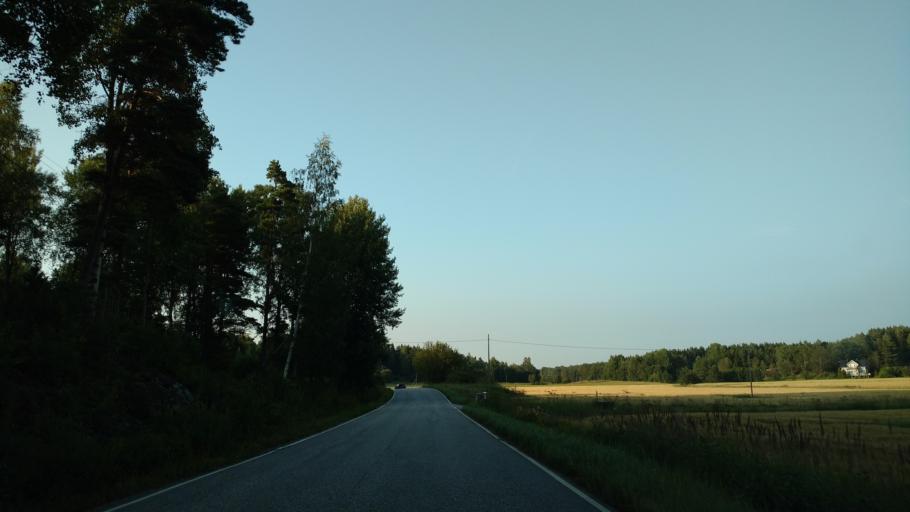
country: FI
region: Varsinais-Suomi
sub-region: Aboland-Turunmaa
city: Dragsfjaerd
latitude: 60.0388
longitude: 22.4431
